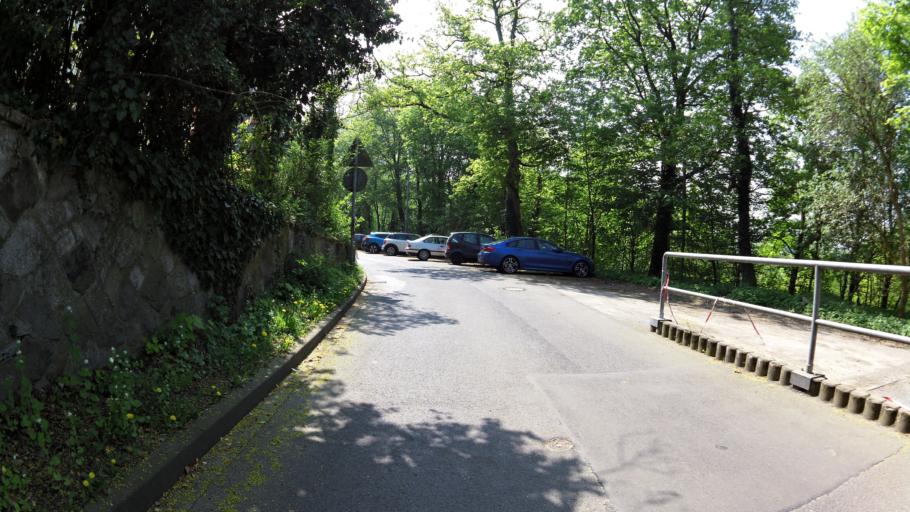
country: DE
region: North Rhine-Westphalia
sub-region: Regierungsbezirk Koln
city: Aachen
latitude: 50.7900
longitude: 6.0708
